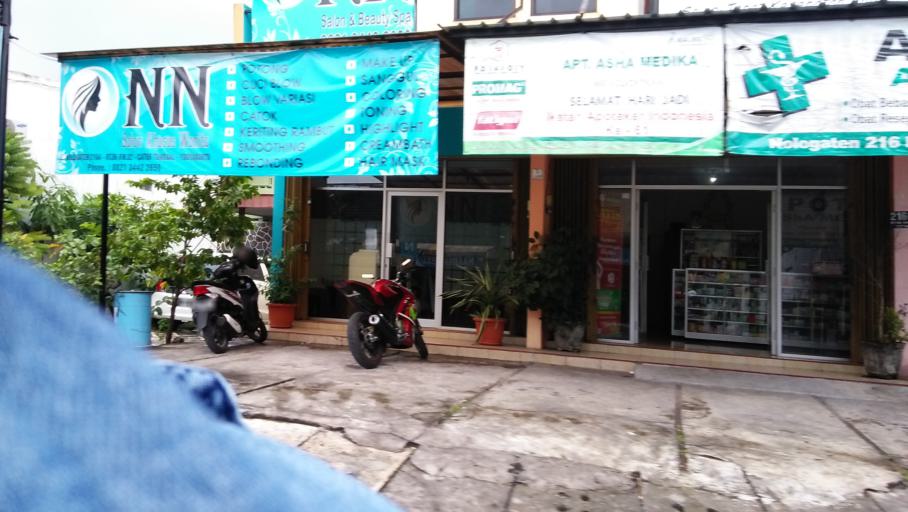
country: ID
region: Daerah Istimewa Yogyakarta
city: Depok
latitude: -7.7776
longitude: 110.4005
